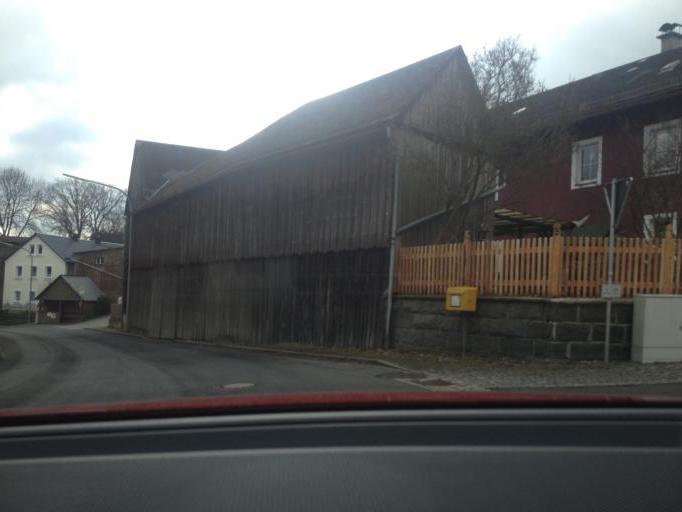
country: DE
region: Bavaria
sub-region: Upper Franconia
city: Thiersheim
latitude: 50.0677
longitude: 12.1517
